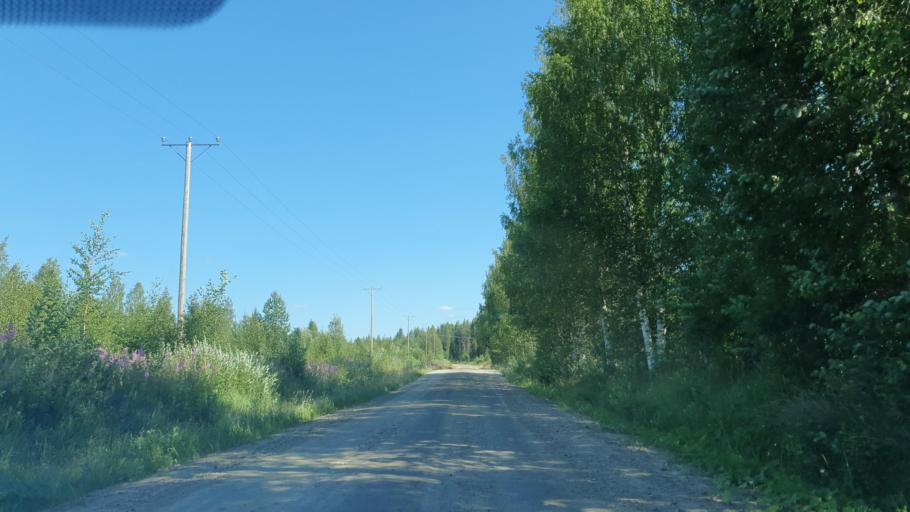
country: FI
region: Kainuu
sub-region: Kehys-Kainuu
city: Kuhmo
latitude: 64.0485
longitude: 29.6201
